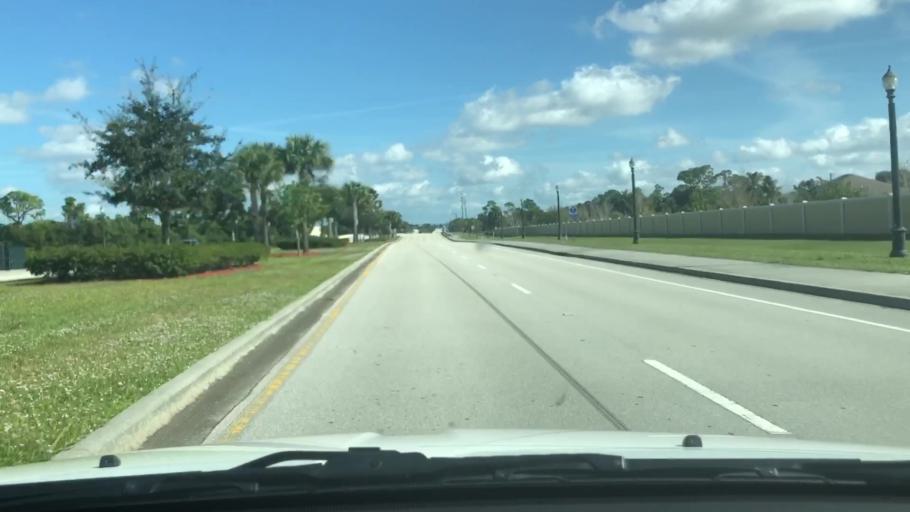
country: US
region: Florida
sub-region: Saint Lucie County
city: Port Saint Lucie
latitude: 27.2945
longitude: -80.4297
